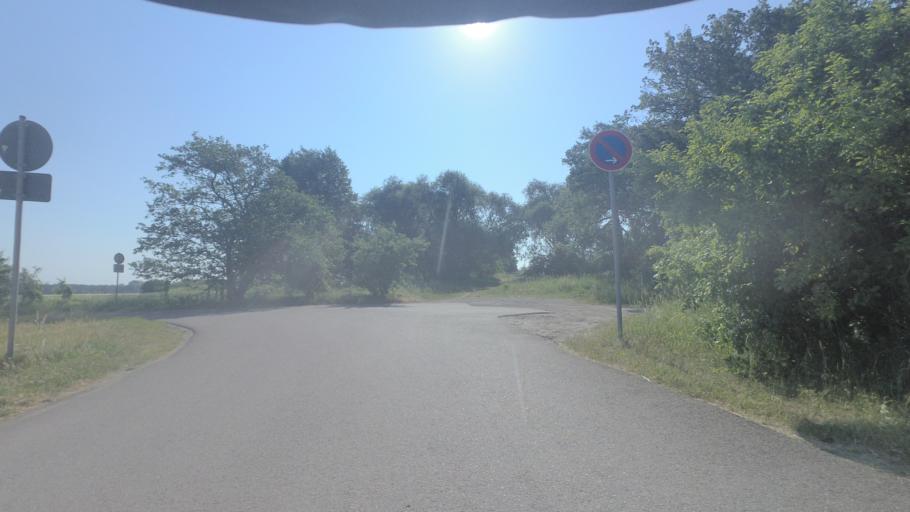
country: DE
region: Saxony-Anhalt
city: Quellendorf
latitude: 51.8169
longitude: 12.1578
